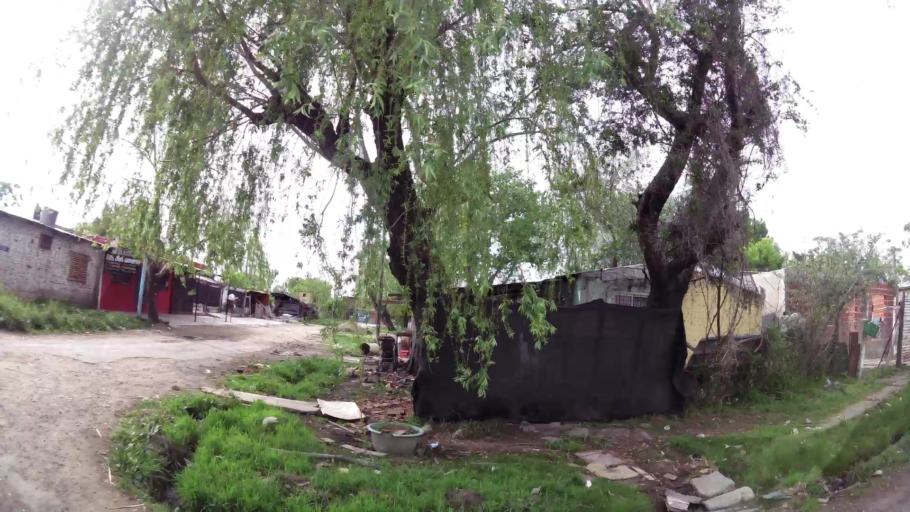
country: AR
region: Buenos Aires
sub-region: Partido de Quilmes
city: Quilmes
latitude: -34.7146
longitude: -58.2398
